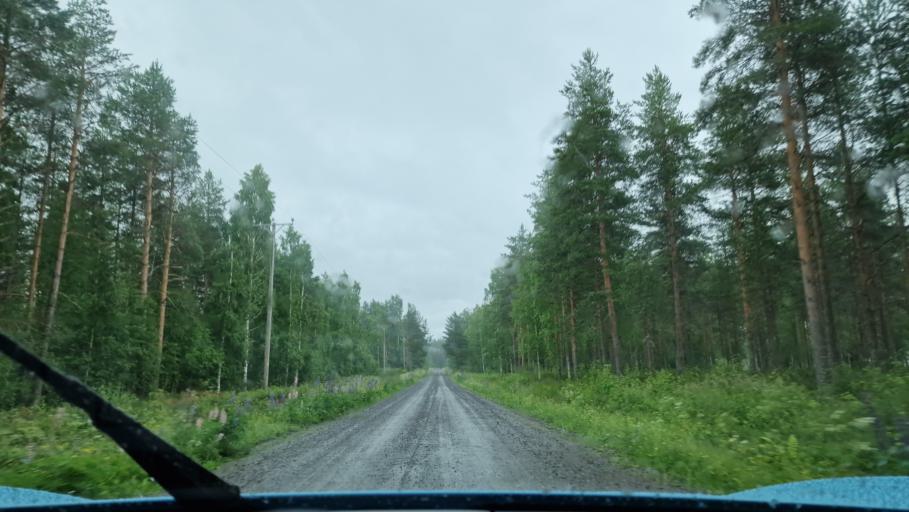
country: FI
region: Southern Ostrobothnia
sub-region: Jaerviseutu
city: Soini
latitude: 62.8463
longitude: 24.3295
